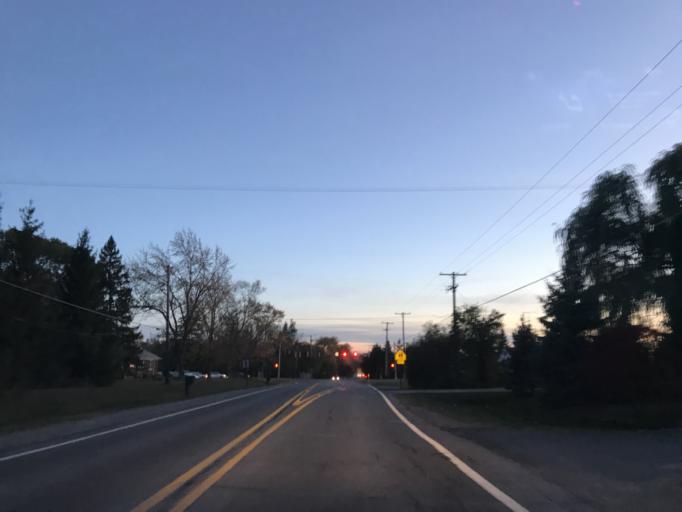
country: US
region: Michigan
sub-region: Oakland County
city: Farmington
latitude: 42.4714
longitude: -83.3671
